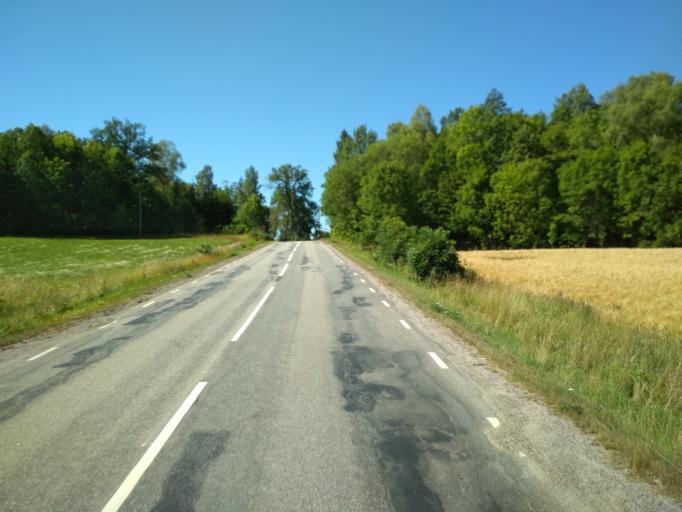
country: SE
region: Soedermanland
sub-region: Strangnas Kommun
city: Mariefred
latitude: 59.2672
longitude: 17.2420
